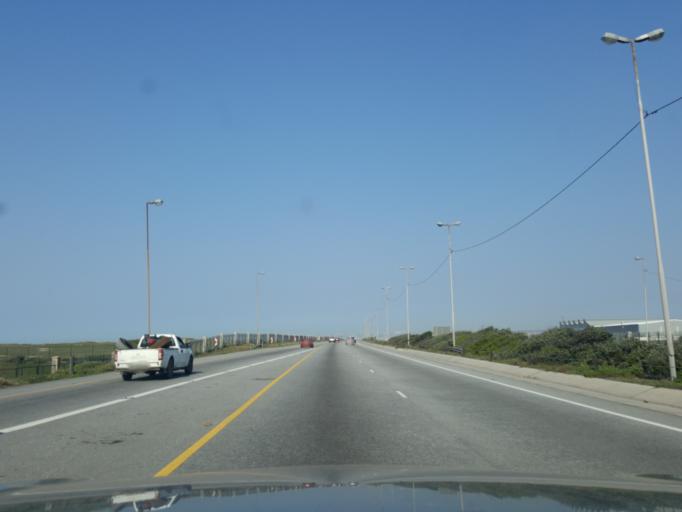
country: ZA
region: Eastern Cape
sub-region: Nelson Mandela Bay Metropolitan Municipality
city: Port Elizabeth
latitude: -33.8850
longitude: 25.6232
